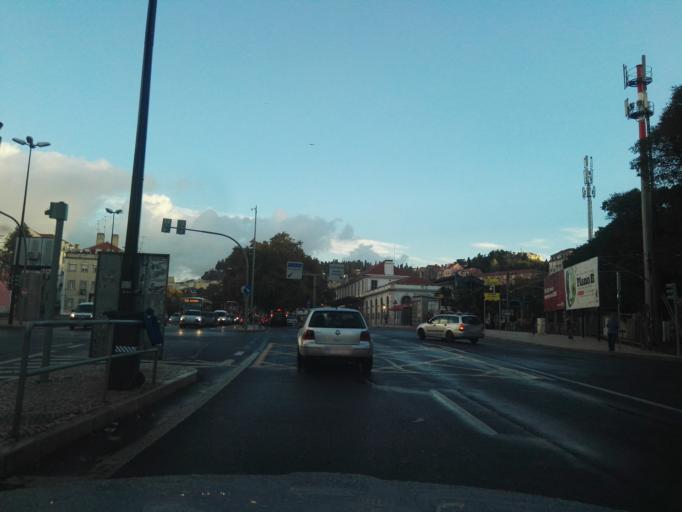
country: PT
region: Setubal
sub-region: Almada
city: Pragal
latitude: 38.7063
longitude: -9.1739
